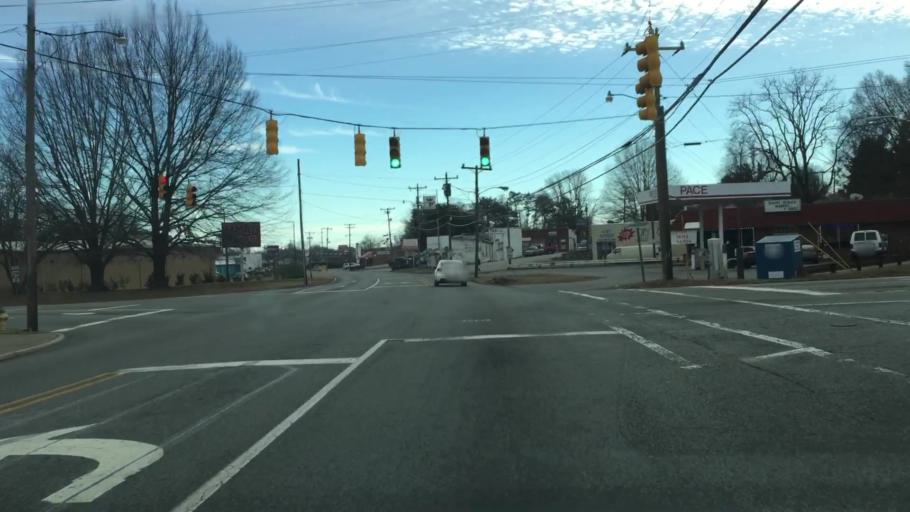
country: US
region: North Carolina
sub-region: Rockingham County
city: Reidsville
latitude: 36.3468
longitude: -79.6652
